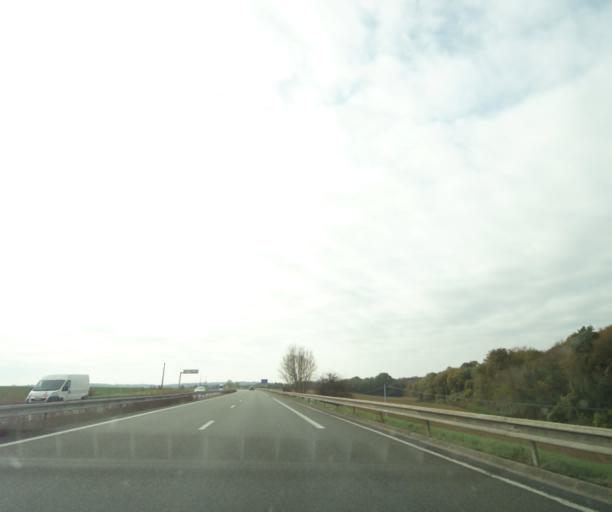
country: FR
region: Ile-de-France
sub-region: Departement de Seine-et-Marne
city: Sammeron
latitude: 48.9699
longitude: 3.0613
